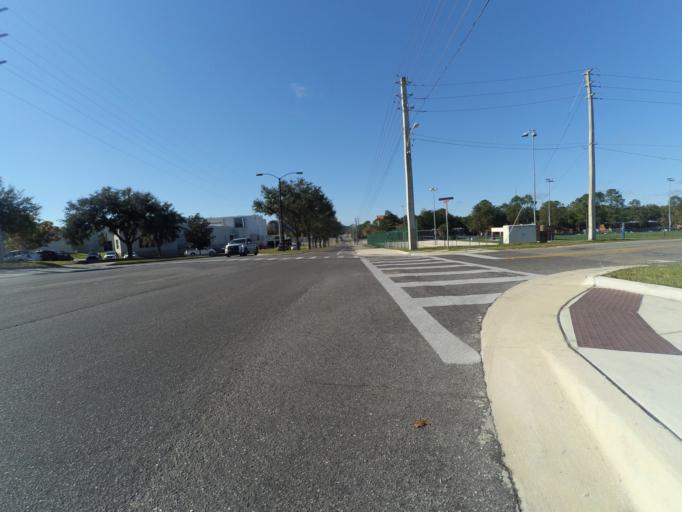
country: US
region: Florida
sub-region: Alachua County
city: Gainesville
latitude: 29.6377
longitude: -82.3690
